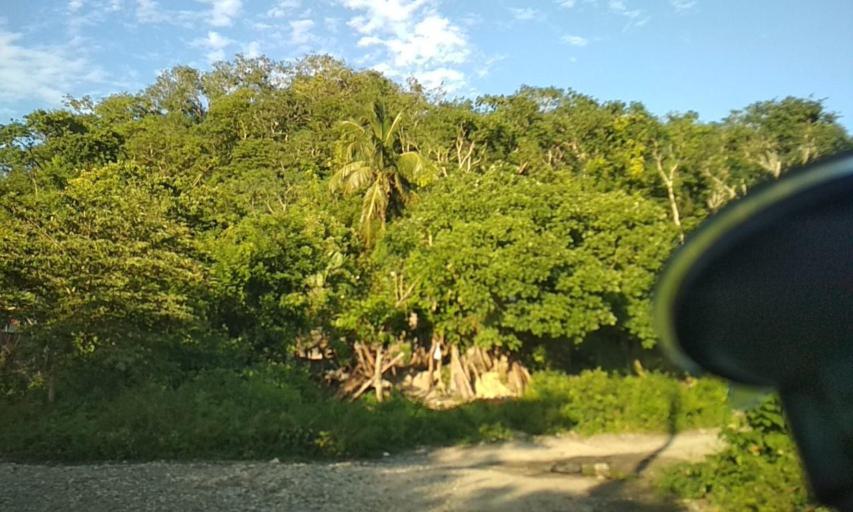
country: MX
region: Veracruz
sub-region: Poza Rica de Hidalgo
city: El Mollejon
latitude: 20.5418
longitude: -97.3996
